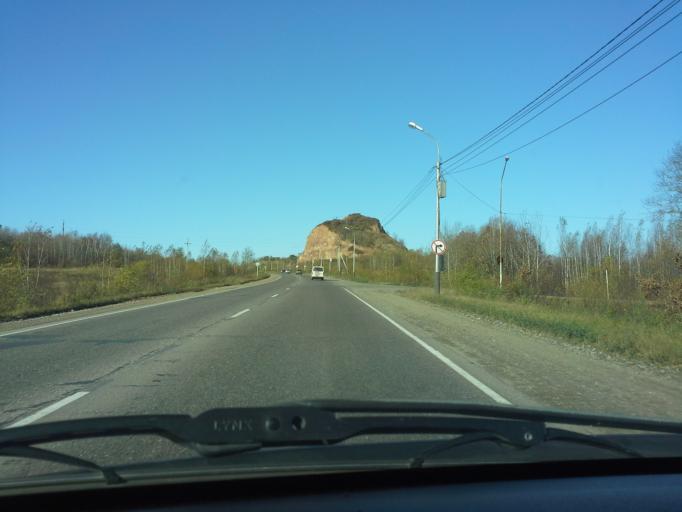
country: RU
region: Khabarovsk Krai
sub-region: Khabarovskiy Rayon
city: Khabarovsk
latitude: 48.5495
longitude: 135.0863
